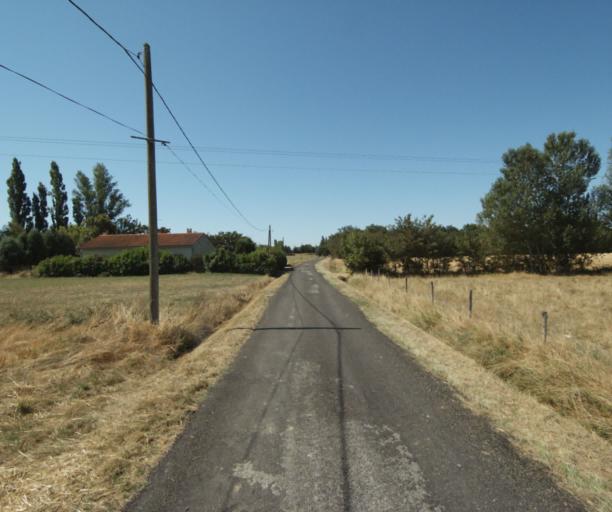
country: FR
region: Midi-Pyrenees
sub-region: Departement de la Haute-Garonne
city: Revel
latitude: 43.4701
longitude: 1.9803
